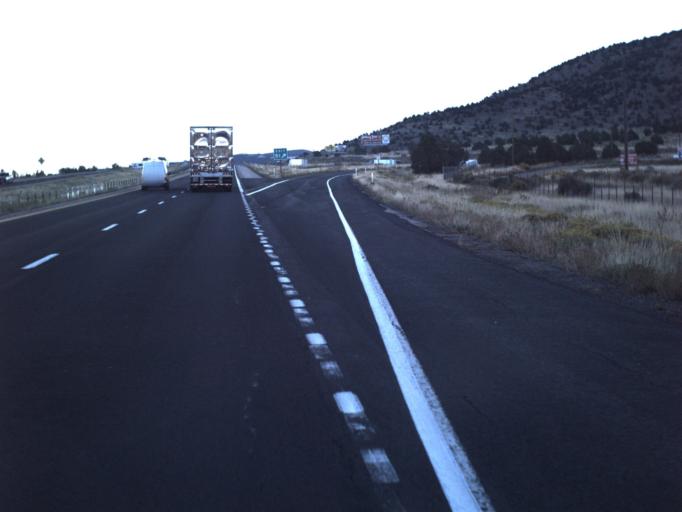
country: US
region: Utah
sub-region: Iron County
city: Cedar City
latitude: 37.5990
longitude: -113.1639
